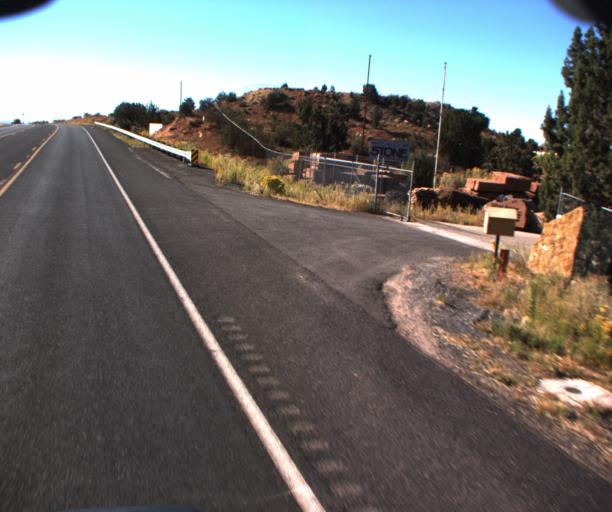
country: US
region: Arizona
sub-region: Coconino County
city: Fredonia
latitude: 36.9937
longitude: -112.5307
